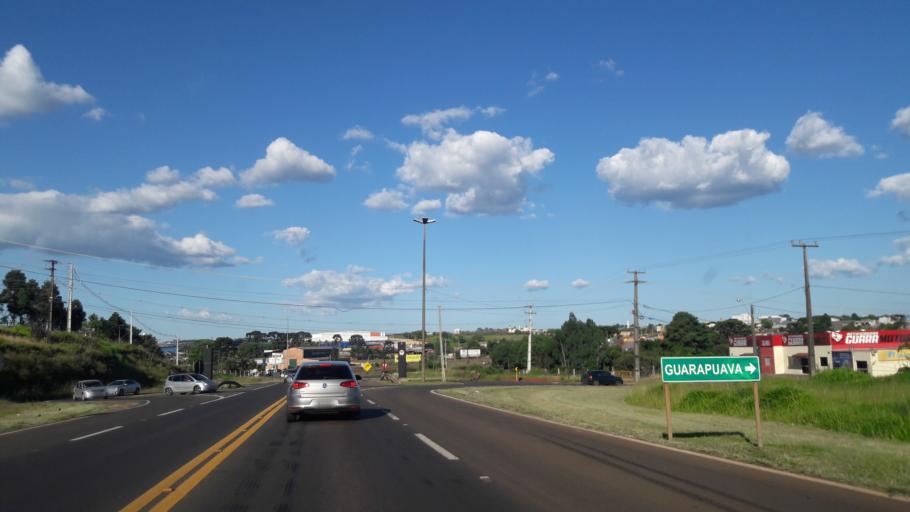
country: BR
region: Parana
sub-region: Guarapuava
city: Guarapuava
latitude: -25.3679
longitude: -51.4942
